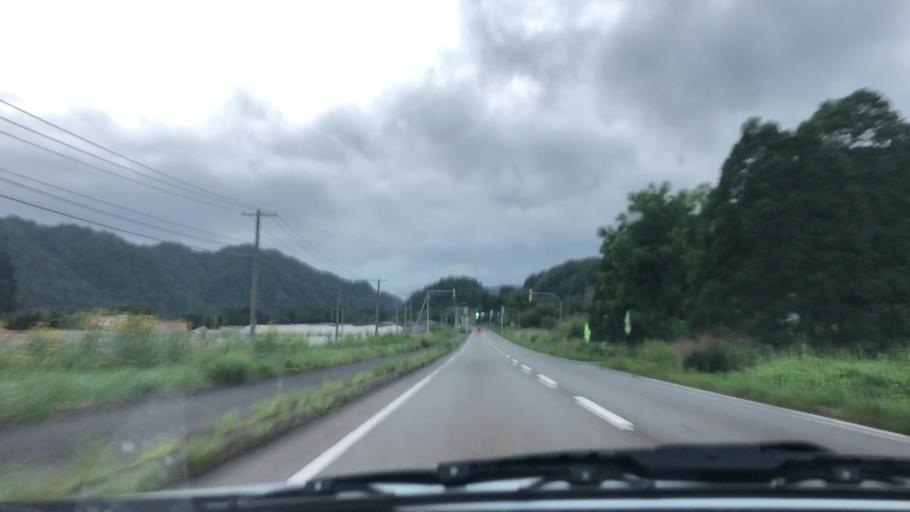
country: JP
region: Hokkaido
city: Chitose
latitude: 42.9054
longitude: 141.9958
